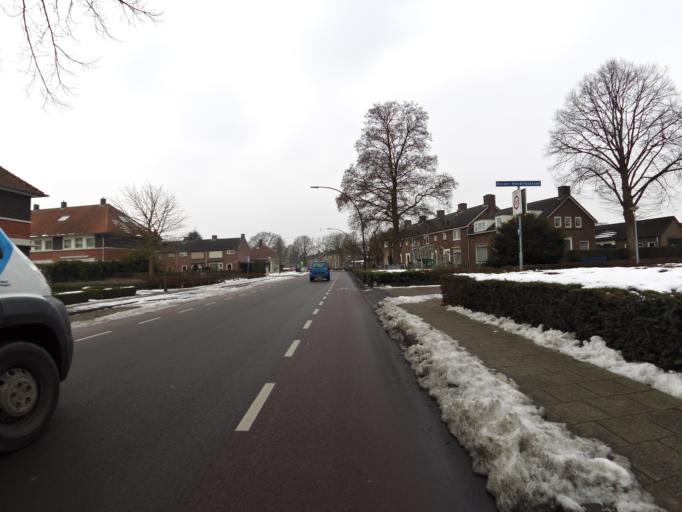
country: NL
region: Gelderland
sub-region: Gemeente Zevenaar
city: Zevenaar
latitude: 51.9312
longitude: 6.0746
